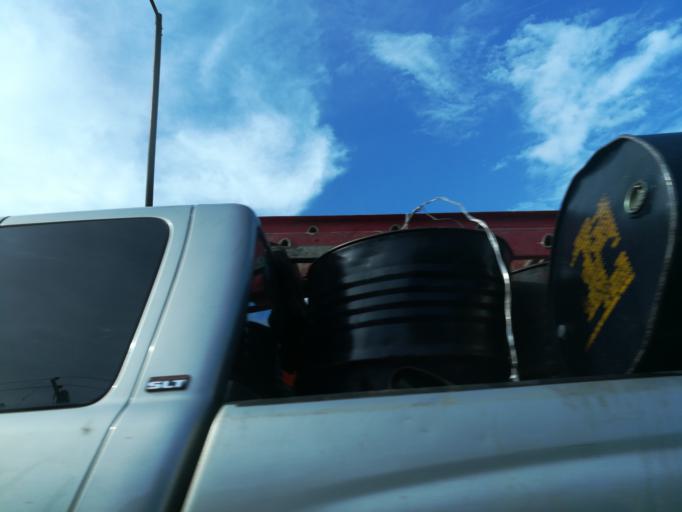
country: NG
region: Lagos
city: Agege
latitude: 6.6007
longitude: 3.3090
